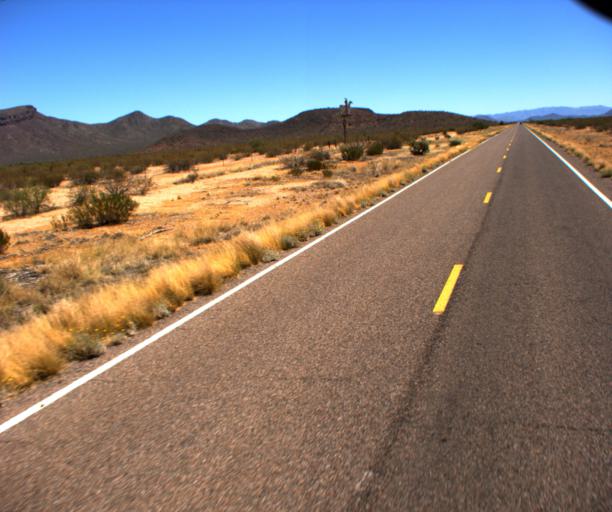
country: US
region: Arizona
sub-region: Yavapai County
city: Congress
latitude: 33.9975
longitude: -113.1249
